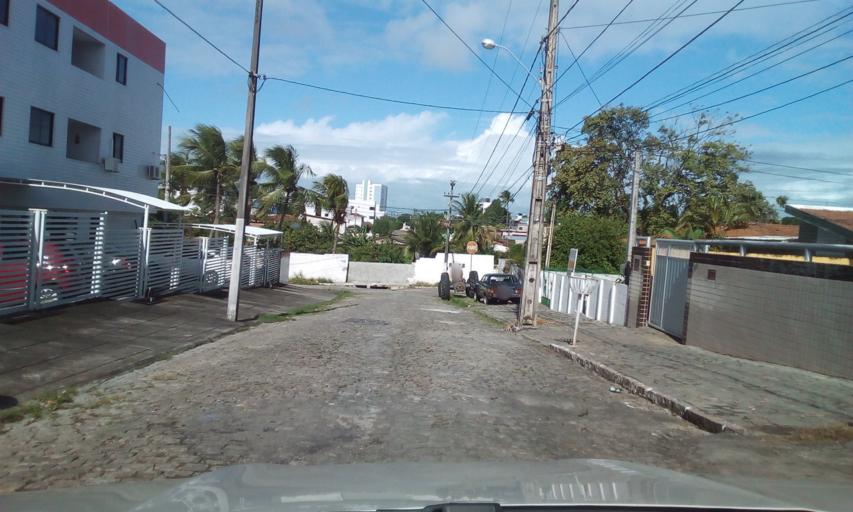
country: BR
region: Paraiba
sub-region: Joao Pessoa
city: Joao Pessoa
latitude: -7.1439
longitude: -34.8392
